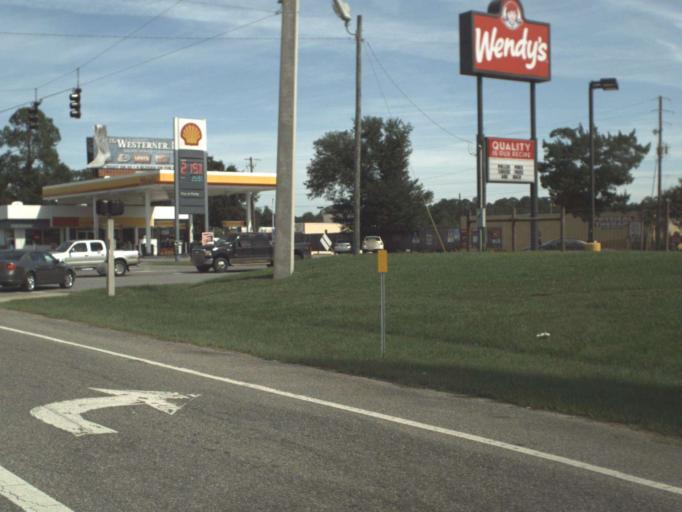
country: US
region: Florida
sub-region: Washington County
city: Chipley
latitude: 30.7512
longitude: -85.5507
